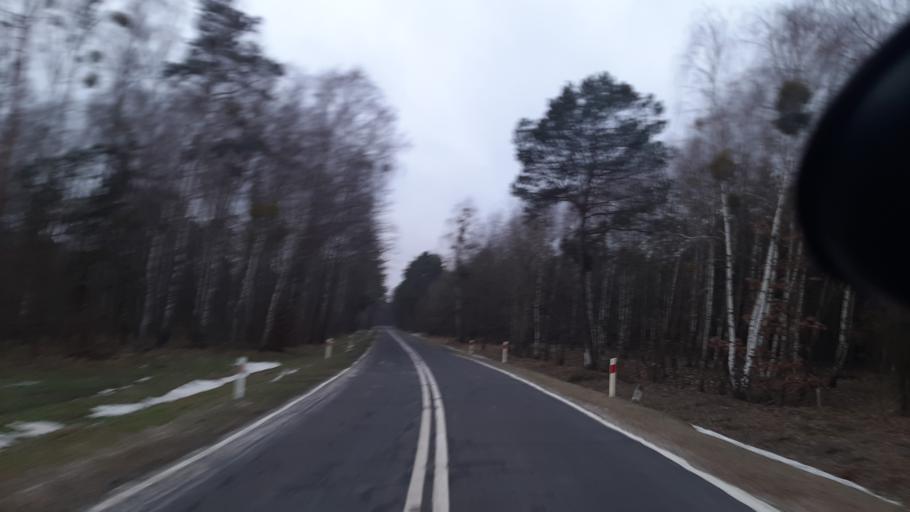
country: PL
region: Lublin Voivodeship
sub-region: Powiat parczewski
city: Podedworze
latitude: 51.5650
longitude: 23.2710
